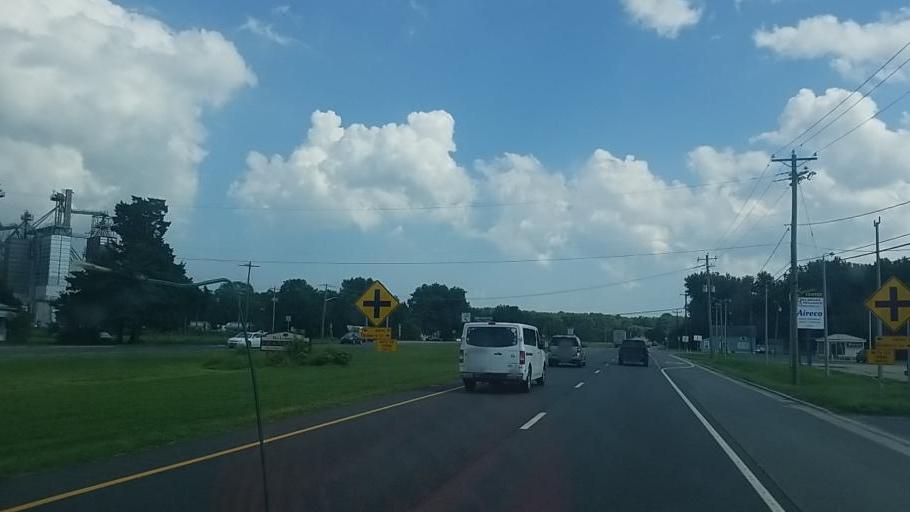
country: US
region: Delaware
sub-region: Sussex County
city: Selbyville
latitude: 38.5185
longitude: -75.2411
